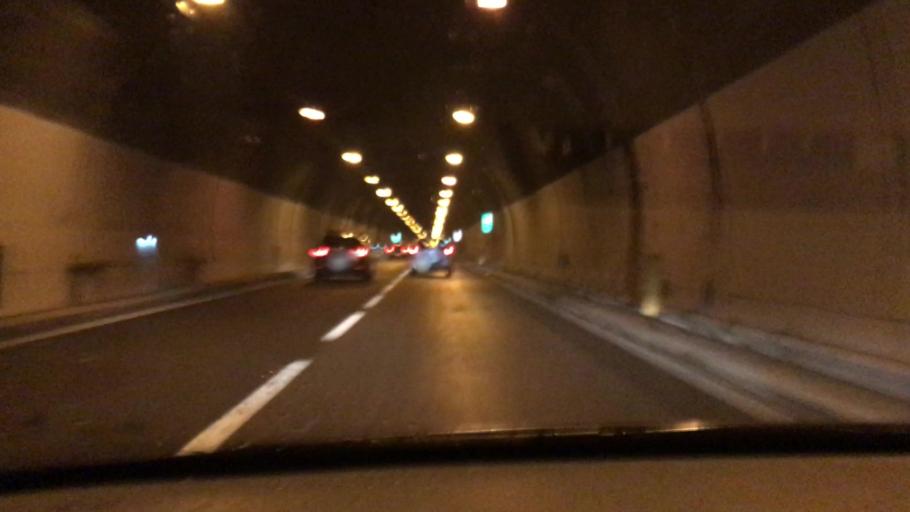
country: IT
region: Lombardy
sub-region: Provincia di Lecco
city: Dervio
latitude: 46.0750
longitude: 9.3154
